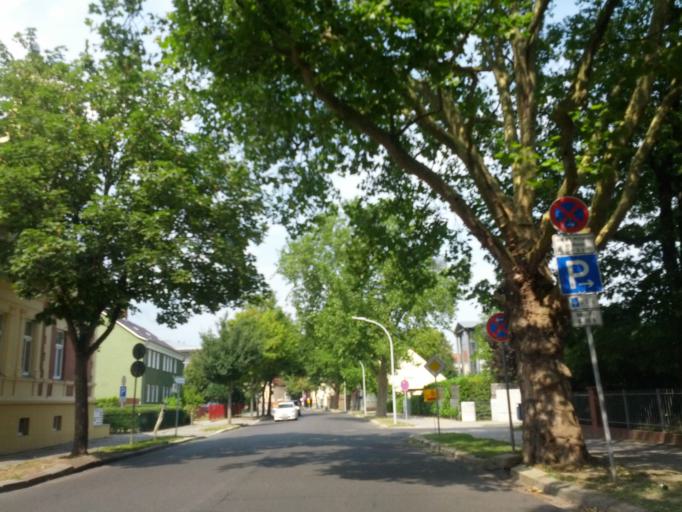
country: DE
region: Brandenburg
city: Nauen
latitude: 52.6021
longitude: 12.8741
